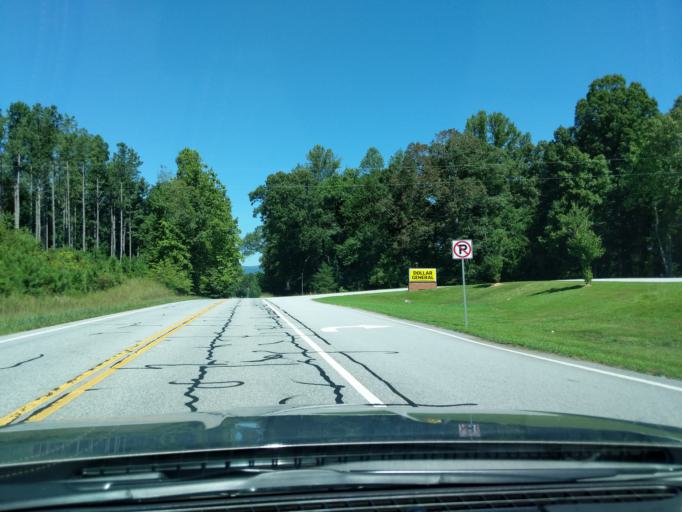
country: US
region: Georgia
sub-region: Habersham County
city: Clarkesville
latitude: 34.6611
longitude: -83.6412
